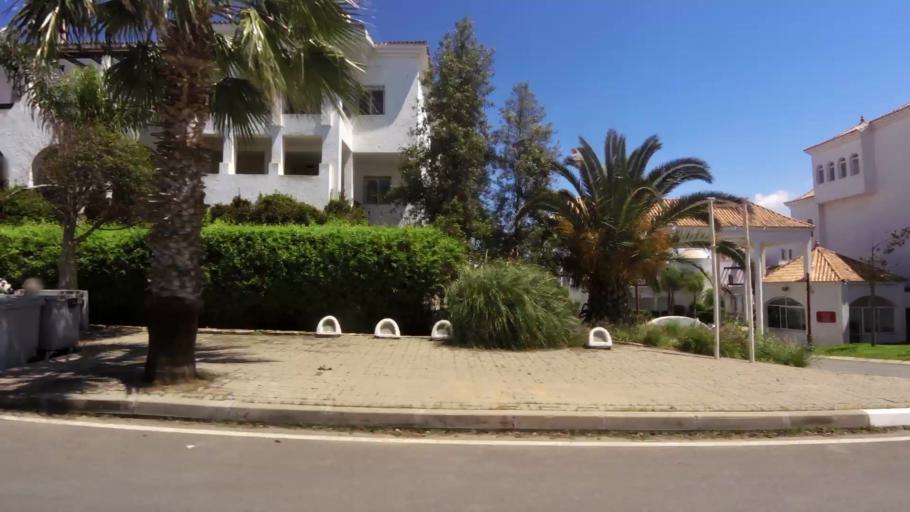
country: MA
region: Grand Casablanca
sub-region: Nouaceur
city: Dar Bouazza
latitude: 33.5287
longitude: -7.8204
